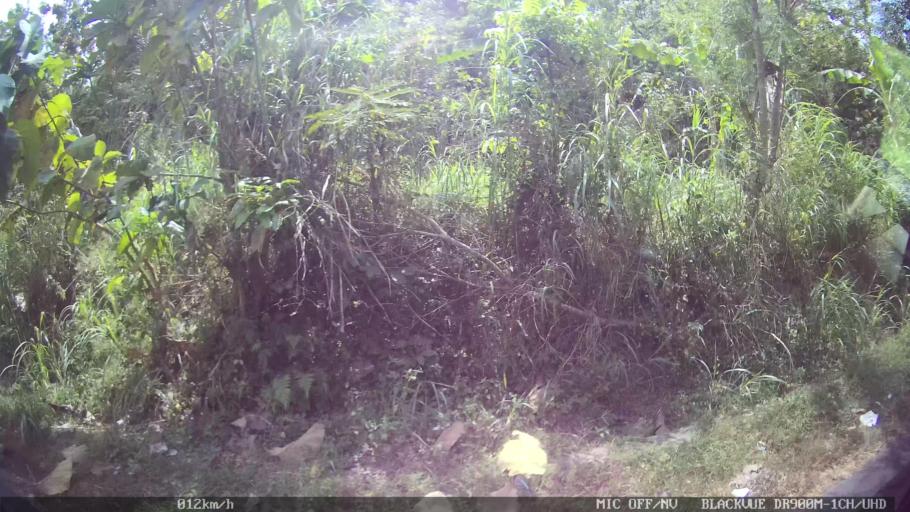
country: ID
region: Central Java
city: Candi Prambanan
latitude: -7.8152
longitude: 110.5143
